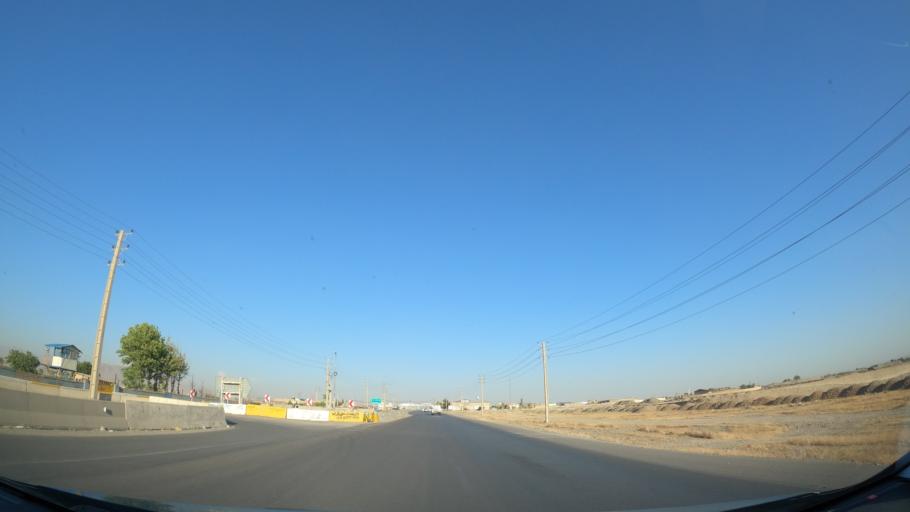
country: IR
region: Alborz
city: Hashtgerd
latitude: 35.9203
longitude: 50.7481
